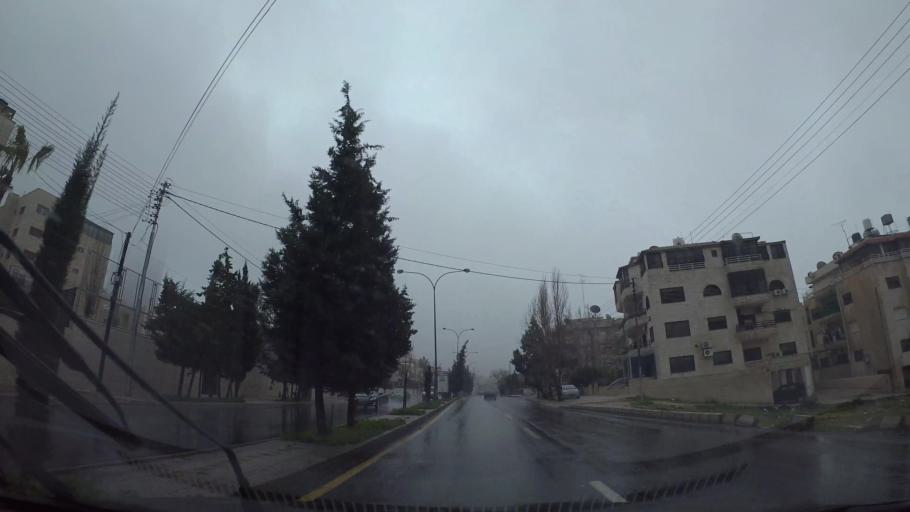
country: JO
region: Amman
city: Wadi as Sir
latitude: 31.9635
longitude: 35.8649
